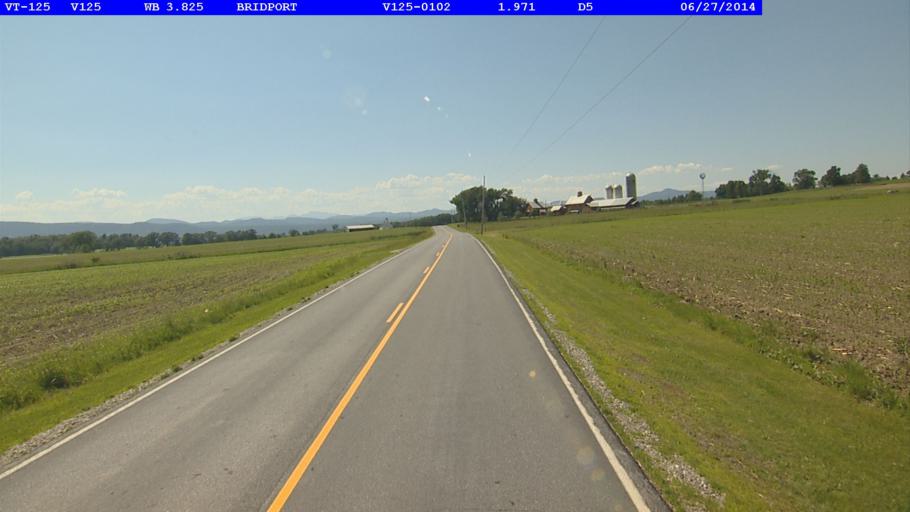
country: US
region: New York
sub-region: Essex County
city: Port Henry
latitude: 44.0028
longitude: -73.3693
